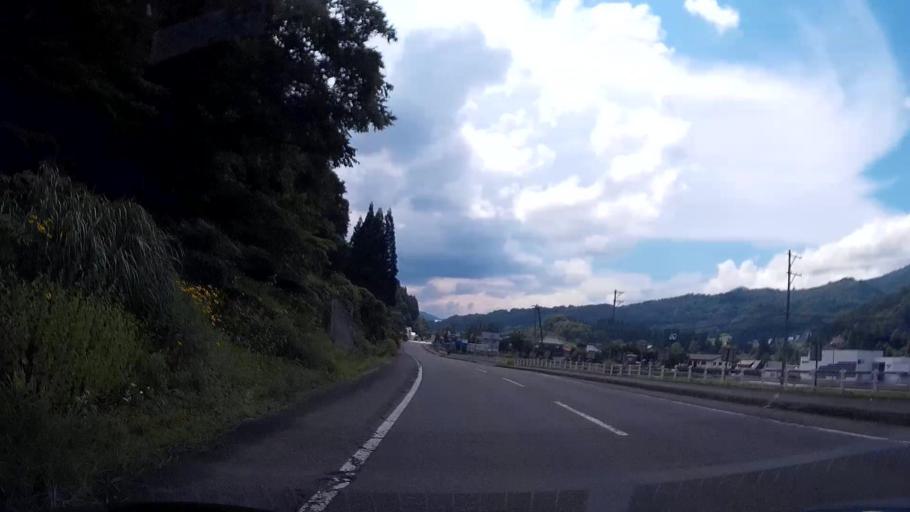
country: JP
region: Niigata
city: Tokamachi
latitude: 36.9959
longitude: 138.5995
